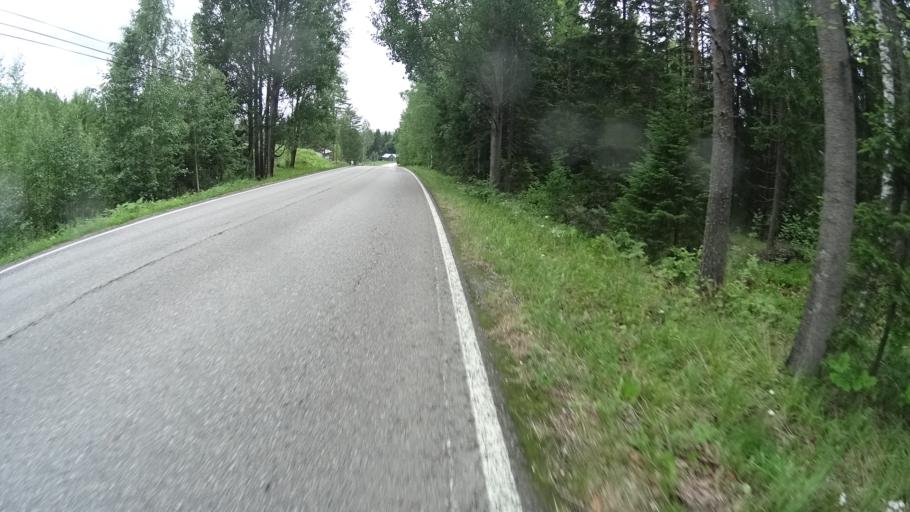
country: FI
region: Uusimaa
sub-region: Helsinki
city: Karkkila
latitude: 60.5714
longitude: 24.3236
